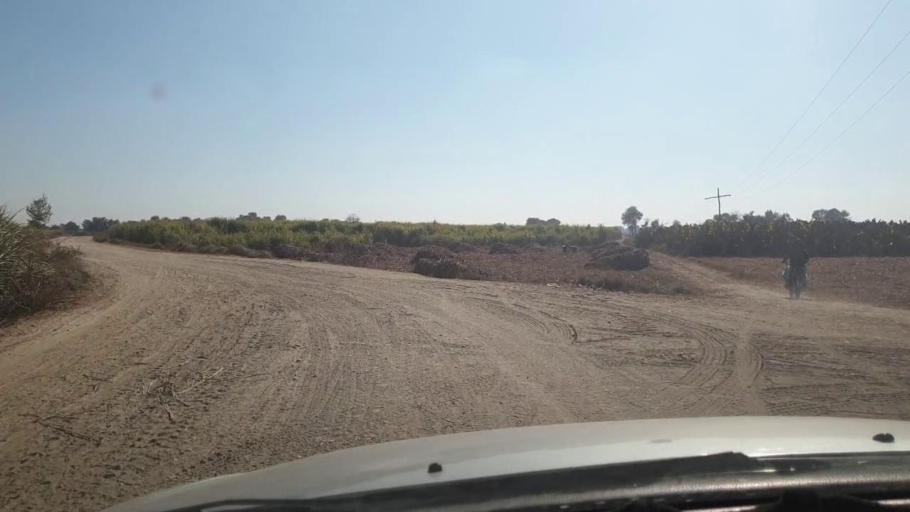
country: PK
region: Sindh
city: Ghotki
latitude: 28.0255
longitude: 69.2191
